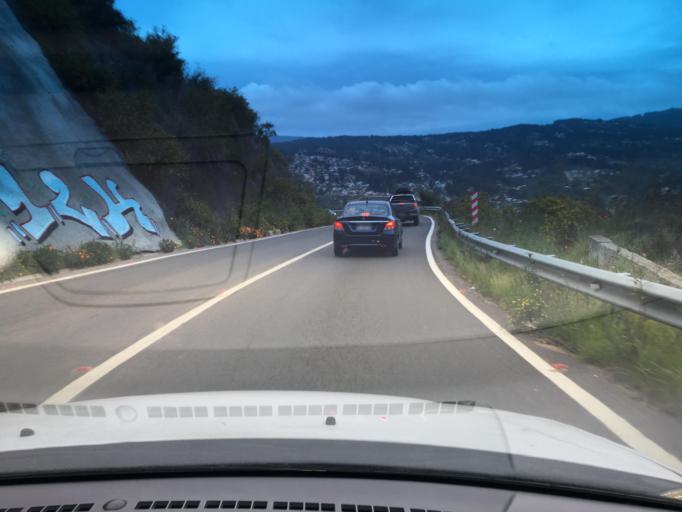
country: CL
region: Valparaiso
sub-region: Provincia de Valparaiso
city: Valparaiso
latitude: -33.0966
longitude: -71.6596
